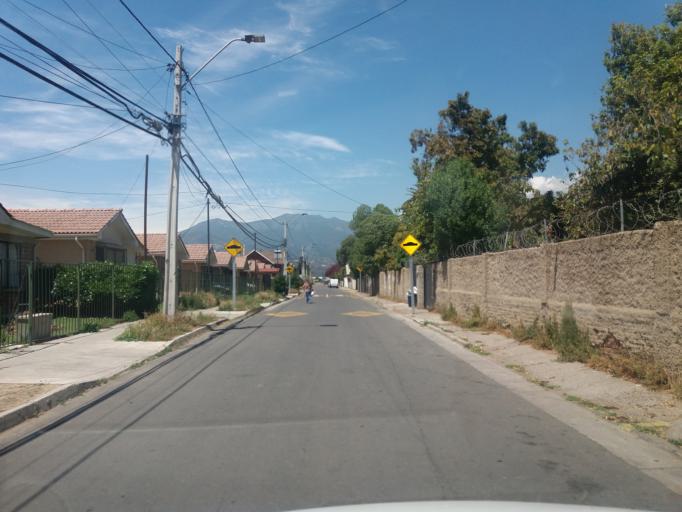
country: CL
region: Valparaiso
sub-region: Provincia de Quillota
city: Quillota
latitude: -32.8547
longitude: -71.2340
